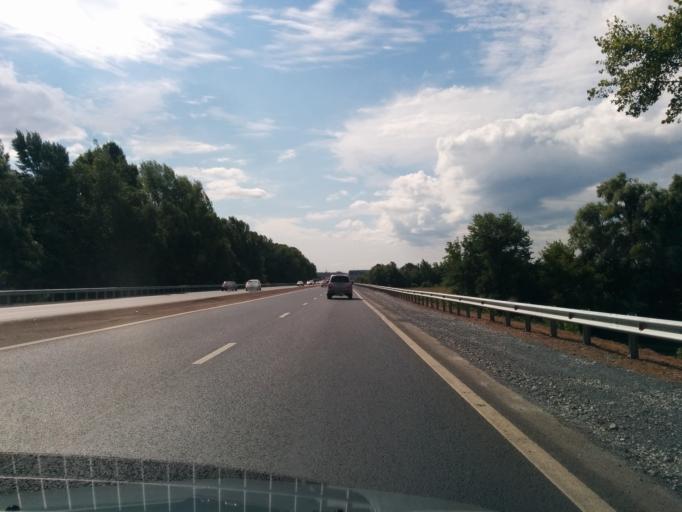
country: RU
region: Bashkortostan
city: Avdon
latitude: 54.5115
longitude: 55.8997
